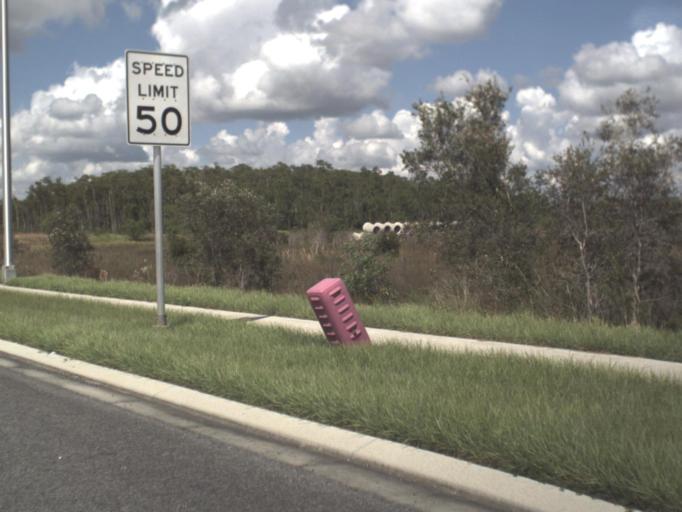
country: US
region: Florida
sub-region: Lee County
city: Gateway
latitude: 26.6210
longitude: -81.7704
